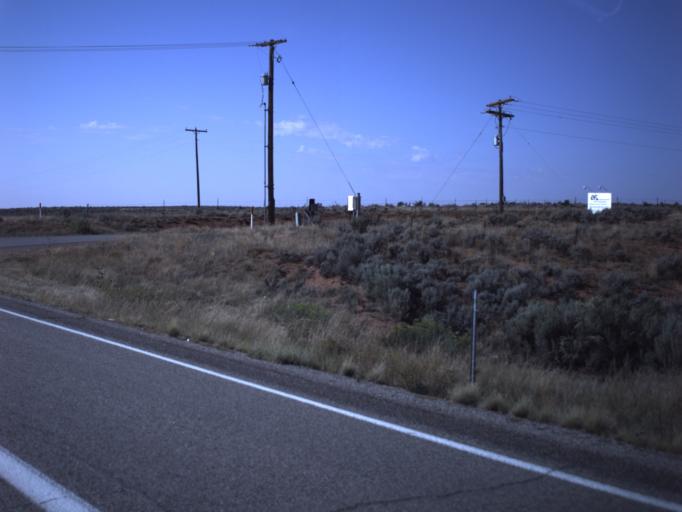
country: US
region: Utah
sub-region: San Juan County
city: Blanding
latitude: 37.5345
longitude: -109.4942
